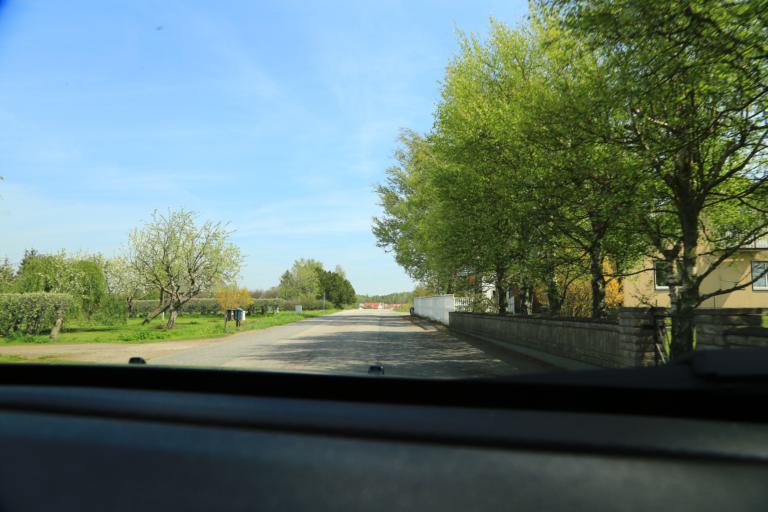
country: SE
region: Halland
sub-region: Varbergs Kommun
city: Varberg
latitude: 57.1479
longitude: 12.2468
